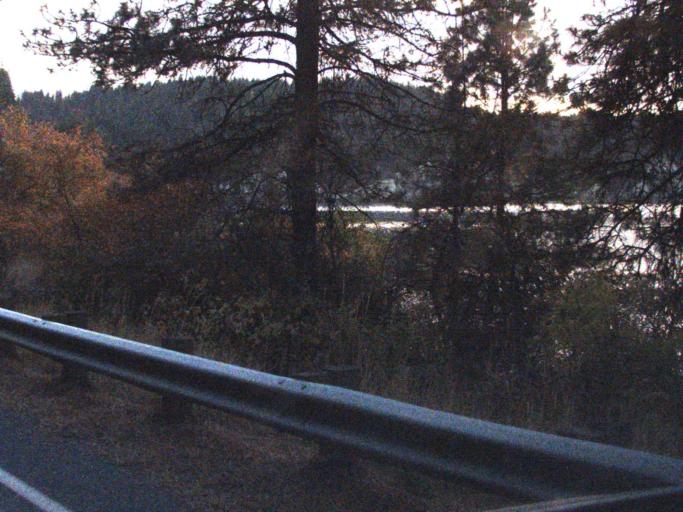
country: US
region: Washington
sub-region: Stevens County
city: Kettle Falls
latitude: 48.6195
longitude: -118.0726
